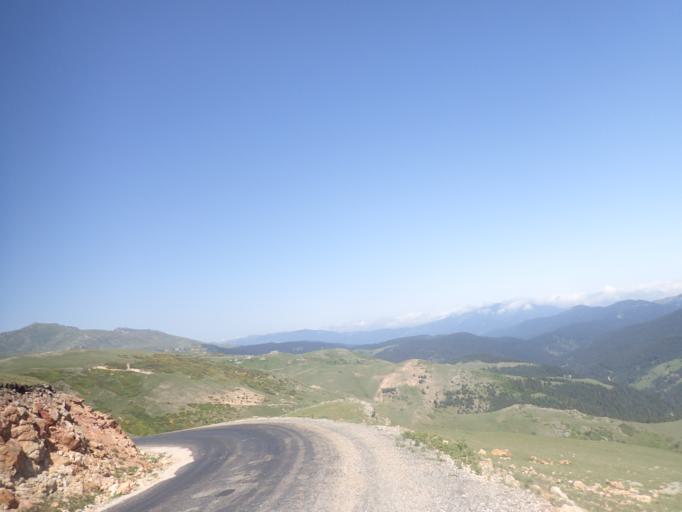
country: TR
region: Ordu
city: Yesilce
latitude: 40.6065
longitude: 37.9211
